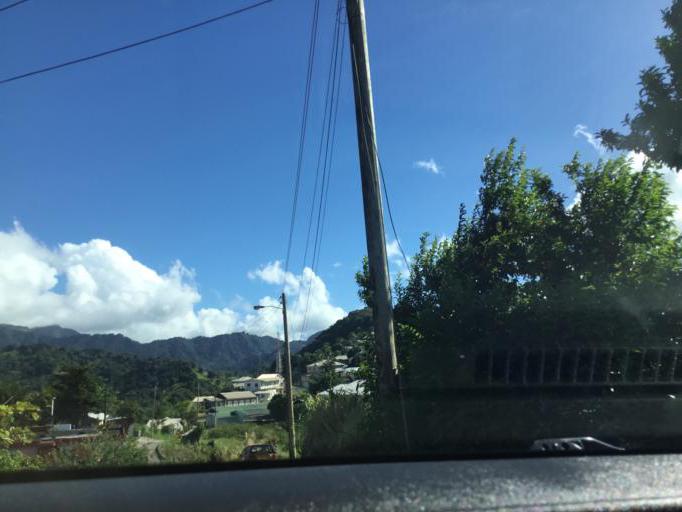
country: VC
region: Saint David
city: Chateaubelair
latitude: 13.2727
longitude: -61.2394
